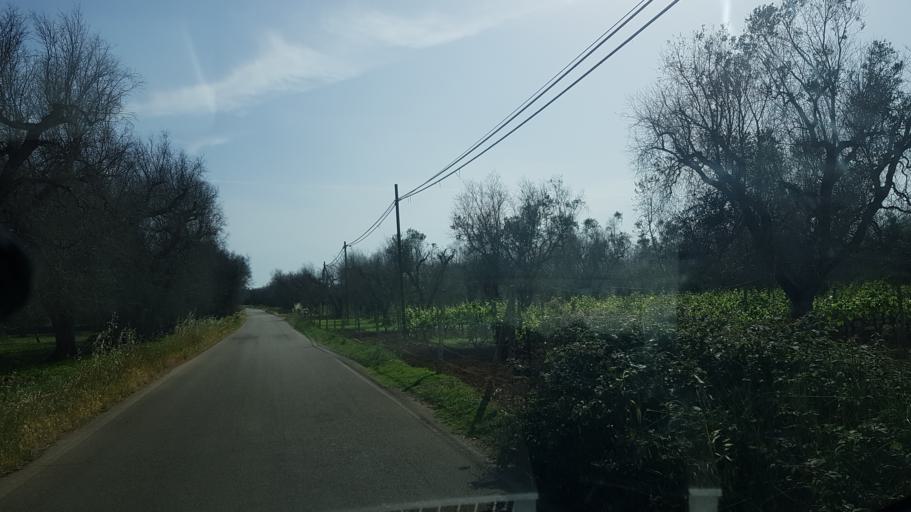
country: IT
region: Apulia
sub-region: Provincia di Brindisi
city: Torchiarolo
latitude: 40.5087
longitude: 18.0713
